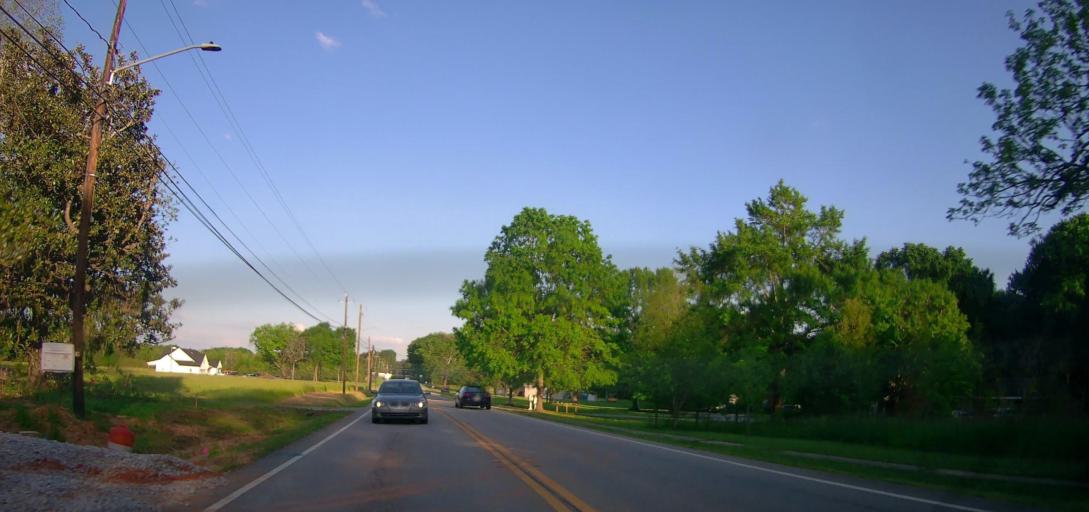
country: US
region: Georgia
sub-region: Walton County
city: Social Circle
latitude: 33.5131
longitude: -83.6900
